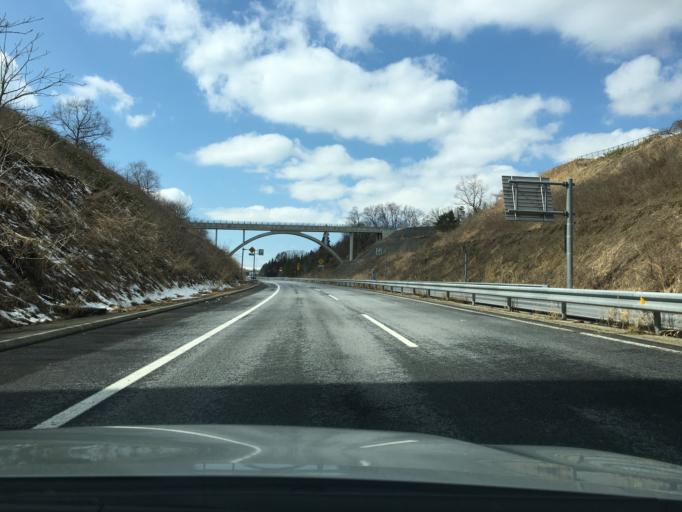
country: JP
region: Yamagata
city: Sagae
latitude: 38.4264
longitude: 140.1592
